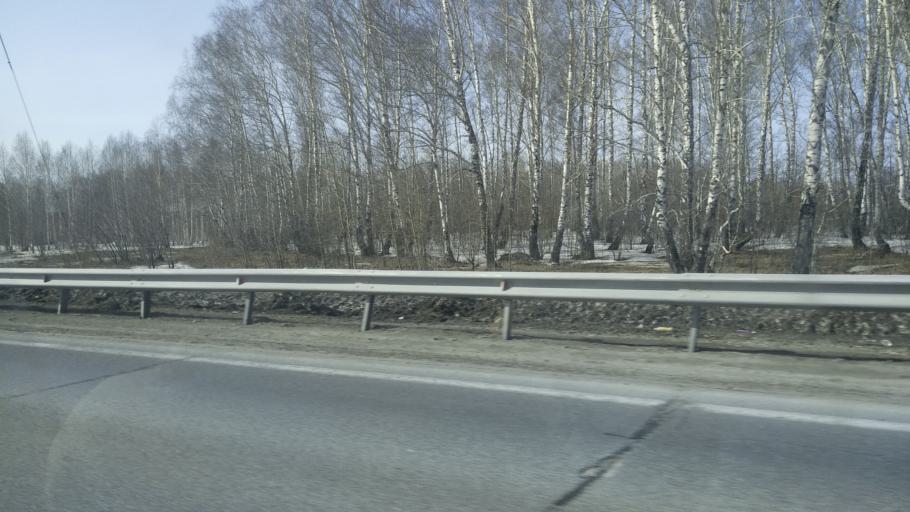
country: RU
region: Novosibirsk
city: Mochishche
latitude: 55.1382
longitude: 83.0117
